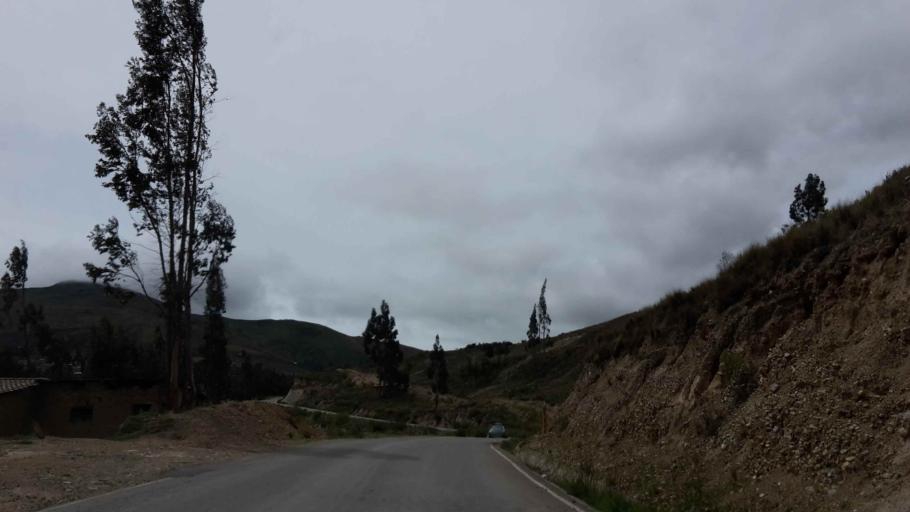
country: BO
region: Cochabamba
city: Colomi
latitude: -17.4001
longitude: -65.8176
